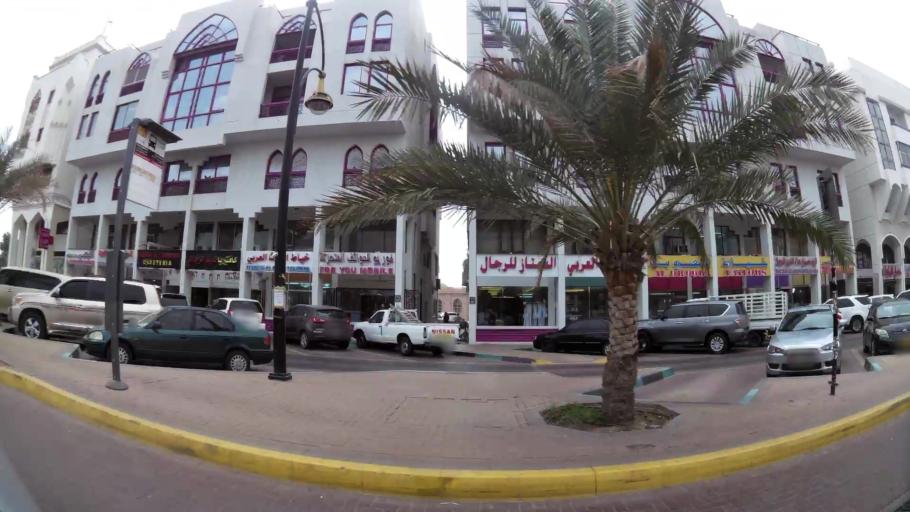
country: AE
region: Abu Dhabi
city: Al Ain
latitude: 24.2281
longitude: 55.7638
